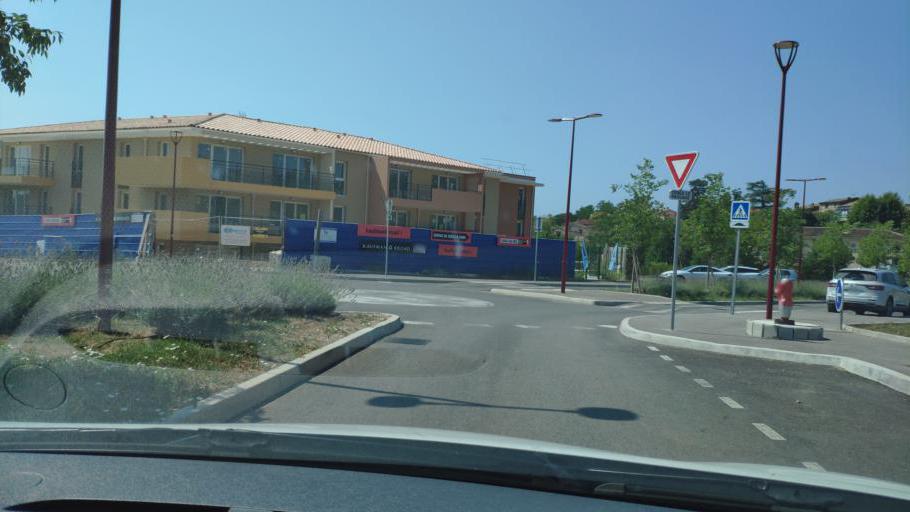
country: FR
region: Provence-Alpes-Cote d'Azur
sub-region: Departement du Var
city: Les Arcs
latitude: 43.4621
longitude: 6.4825
